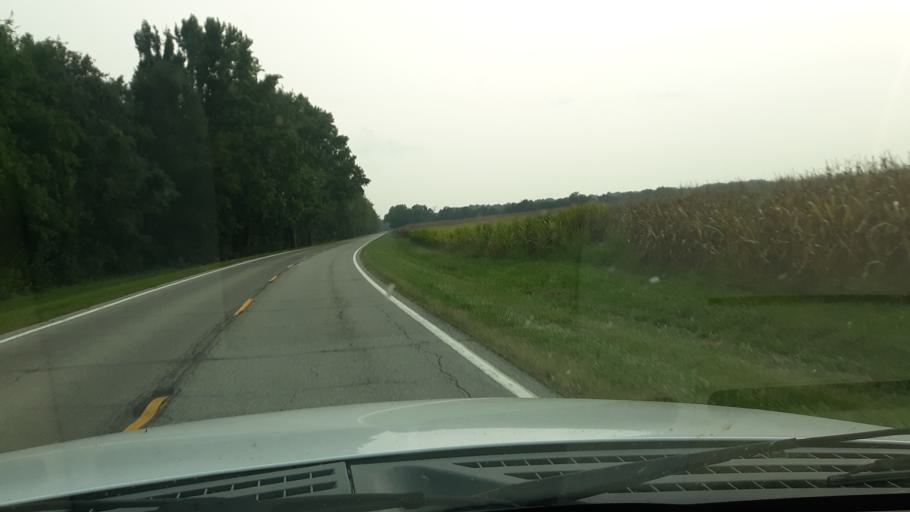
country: US
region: Illinois
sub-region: Edwards County
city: Grayville
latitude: 38.3068
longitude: -87.9438
